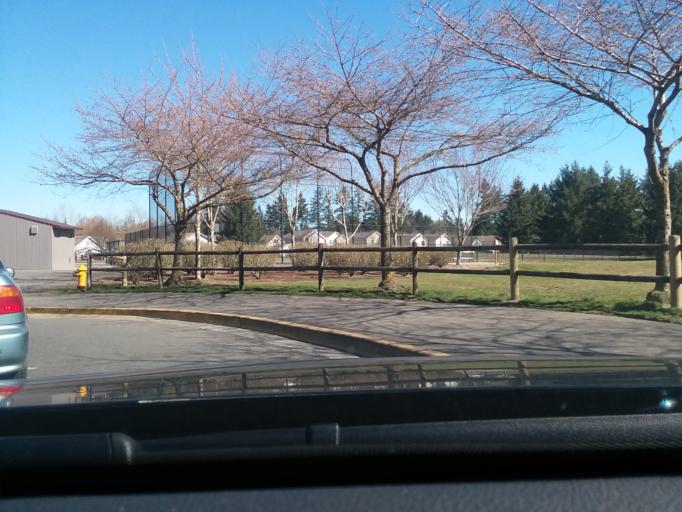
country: US
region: Washington
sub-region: Pierce County
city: Puyallup
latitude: 47.1626
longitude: -122.2860
